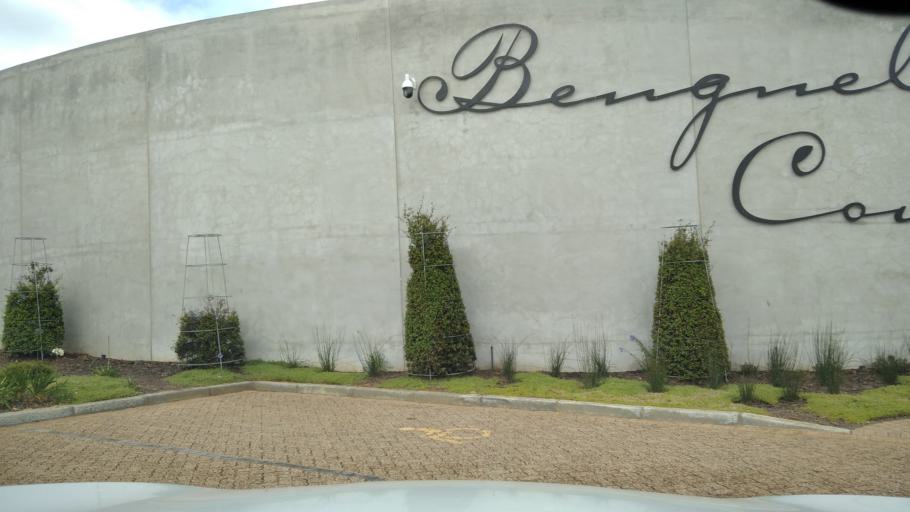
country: ZA
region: Western Cape
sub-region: Overberg District Municipality
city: Hermanus
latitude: -34.3460
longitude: 19.1350
